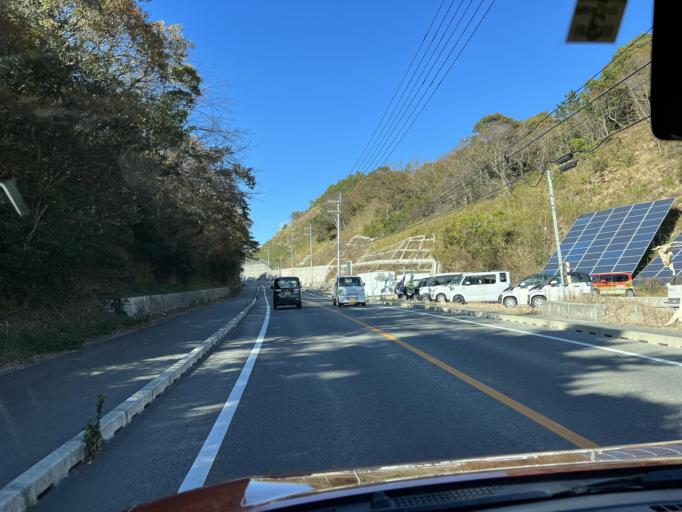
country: JP
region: Kagawa
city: Tonosho
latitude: 34.4726
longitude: 134.2572
